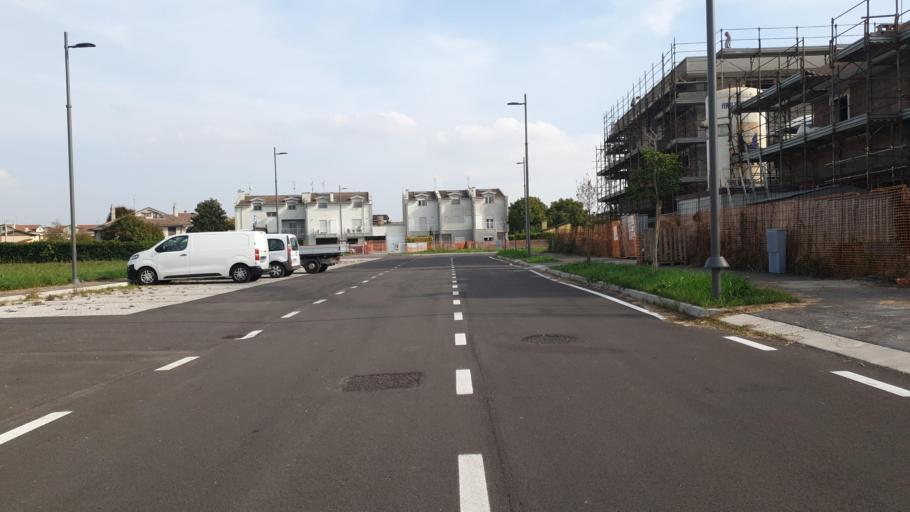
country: IT
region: Veneto
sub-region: Provincia di Padova
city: Albignasego
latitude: 45.3375
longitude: 11.9014
